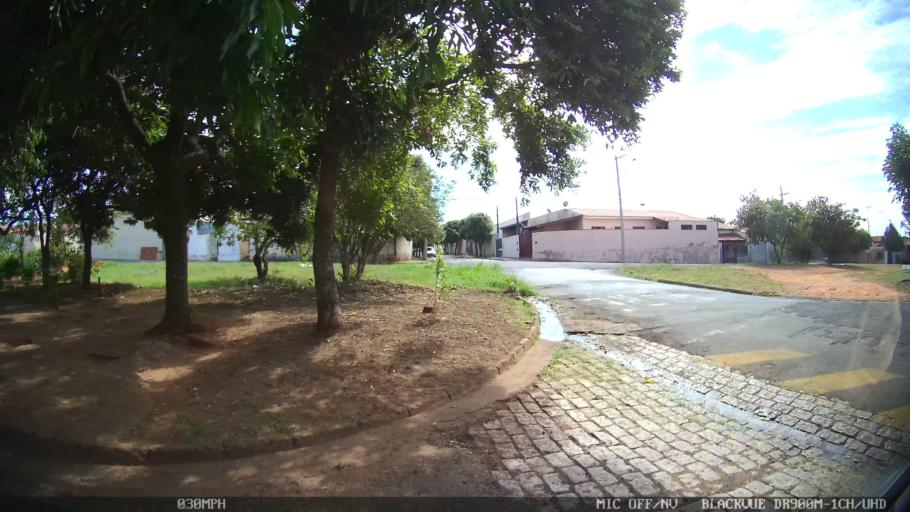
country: BR
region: Sao Paulo
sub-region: Sao Jose Do Rio Preto
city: Sao Jose do Rio Preto
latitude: -20.8339
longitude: -49.3503
